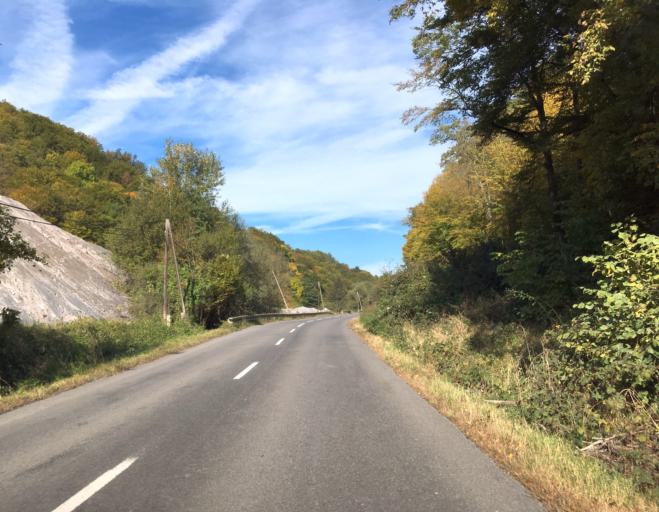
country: SK
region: Banskobystricky
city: Krupina
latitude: 48.3188
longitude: 18.9781
